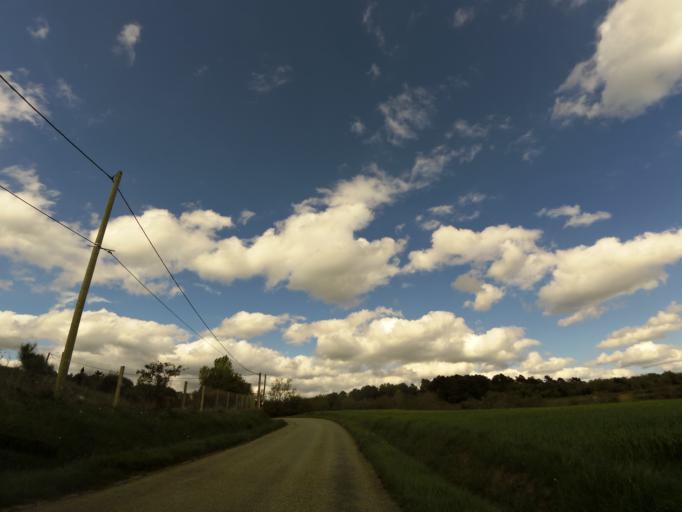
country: FR
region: Languedoc-Roussillon
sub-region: Departement de l'Aude
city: Saint-Martin-Lalande
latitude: 43.3367
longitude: 2.0509
